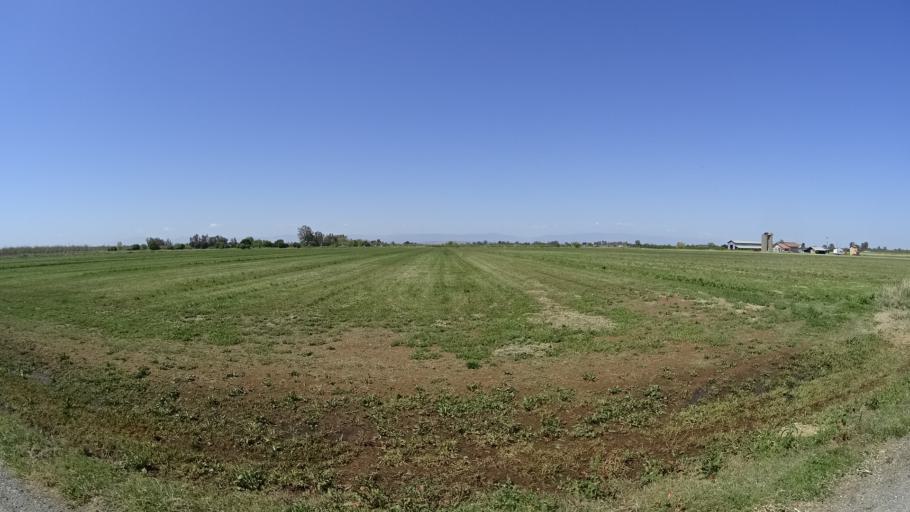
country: US
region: California
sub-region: Glenn County
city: Orland
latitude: 39.7743
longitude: -122.1690
